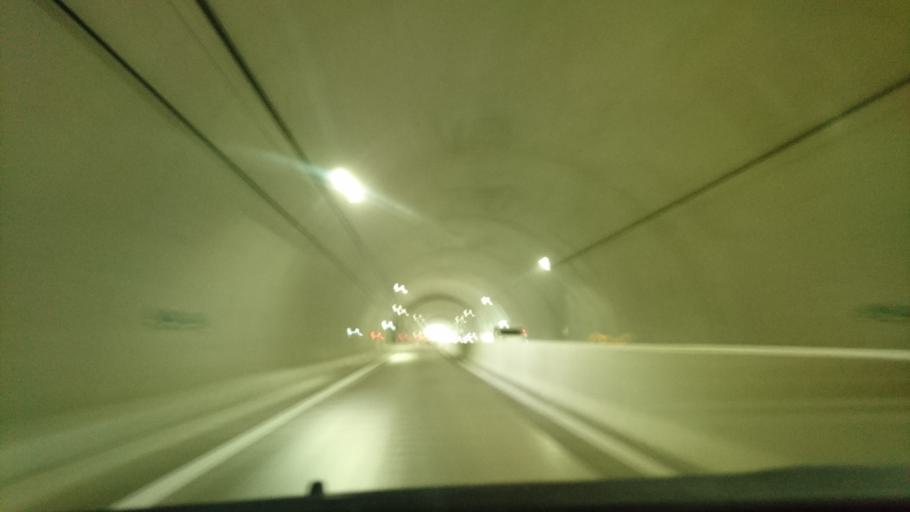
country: JP
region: Iwate
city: Ofunato
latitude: 38.9705
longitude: 141.6240
